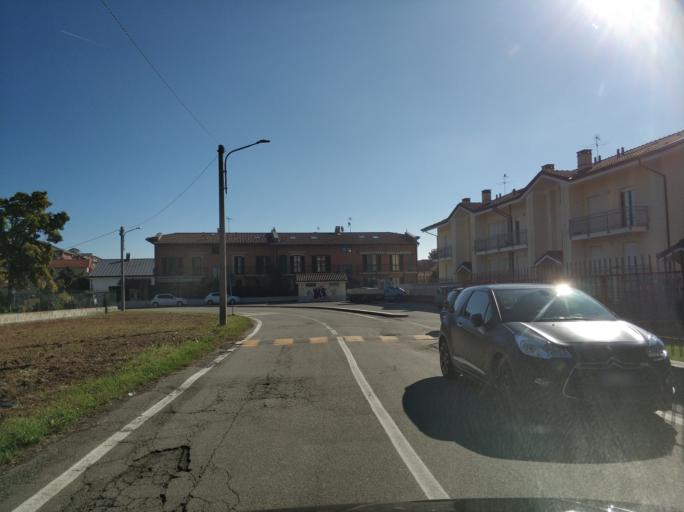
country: IT
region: Piedmont
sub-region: Provincia di Torino
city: Nole
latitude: 45.2451
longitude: 7.5652
